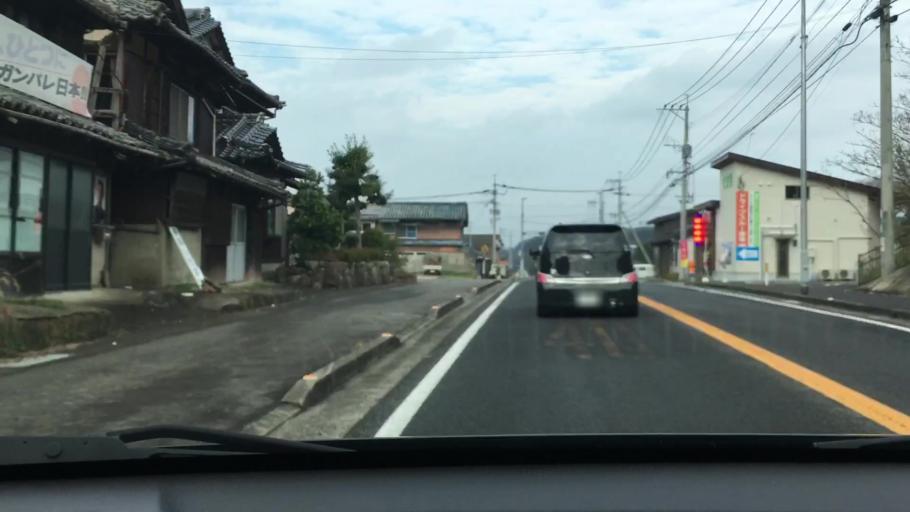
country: JP
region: Saga Prefecture
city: Imaricho-ko
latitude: 33.3101
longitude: 129.9279
